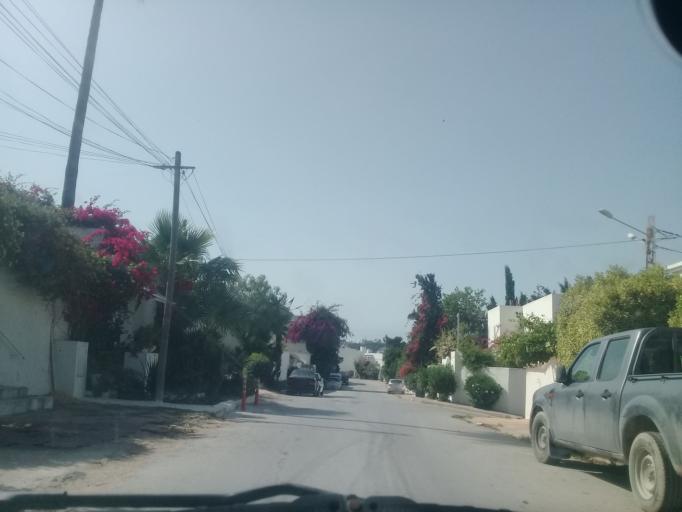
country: TN
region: Tunis
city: Al Marsa
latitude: 36.8894
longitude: 10.3251
